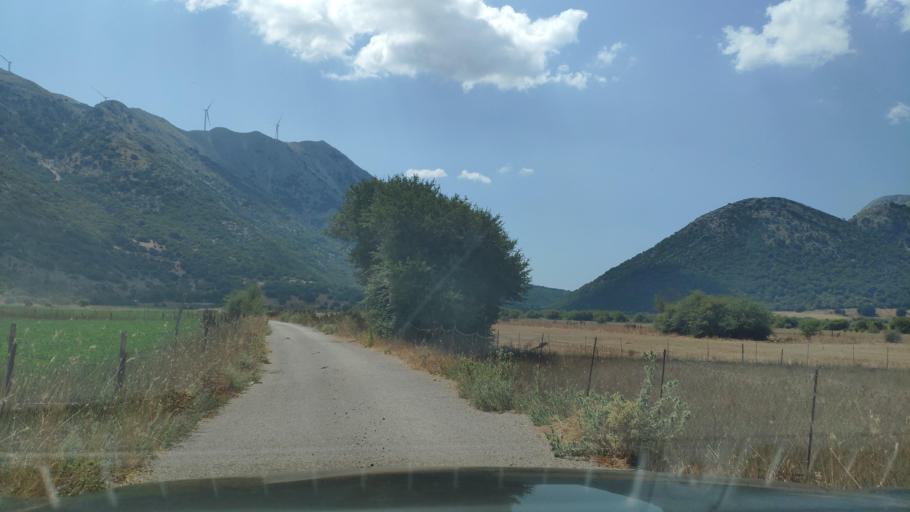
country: GR
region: West Greece
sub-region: Nomos Aitolias kai Akarnanias
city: Monastirakion
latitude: 38.7839
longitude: 20.9682
